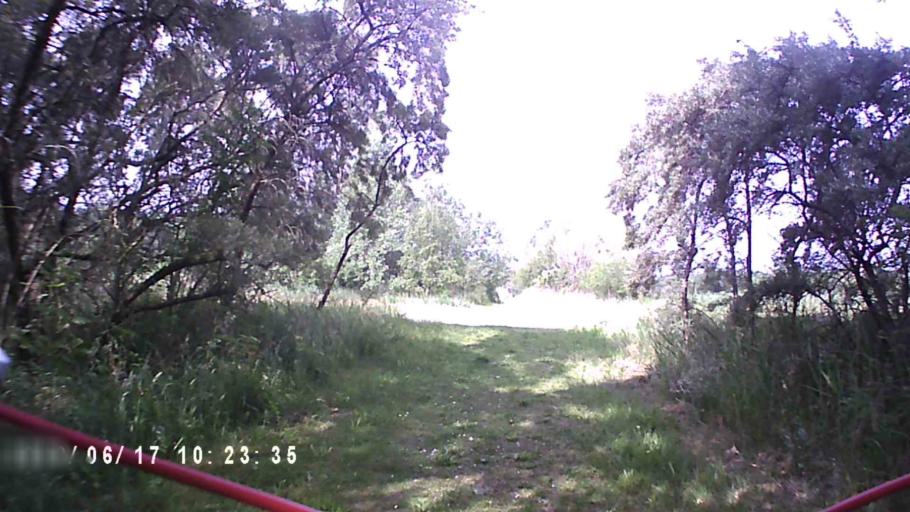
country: NL
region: Groningen
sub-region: Gemeente De Marne
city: Ulrum
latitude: 53.3905
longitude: 6.2480
